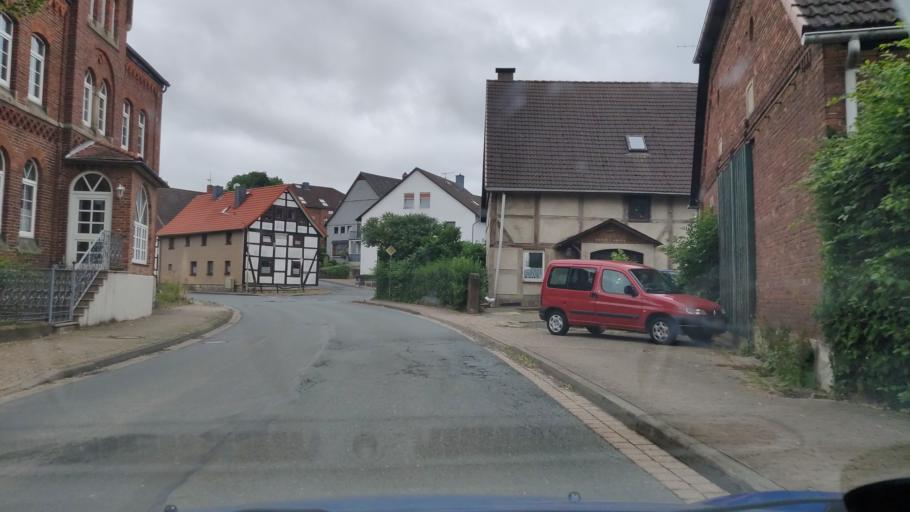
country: DE
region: Lower Saxony
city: Coppenbrugge
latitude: 52.0832
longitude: 9.5020
